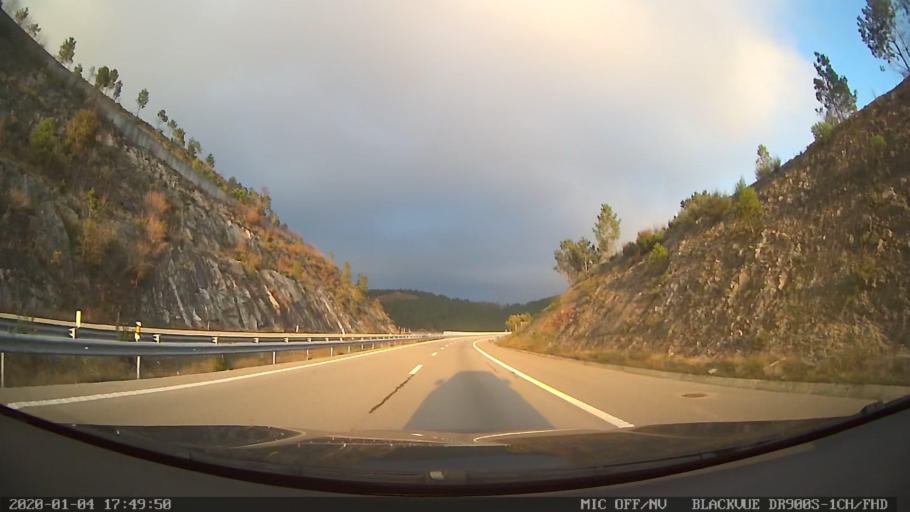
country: PT
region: Vila Real
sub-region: Ribeira de Pena
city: Ribeira de Pena
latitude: 41.4911
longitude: -7.8407
